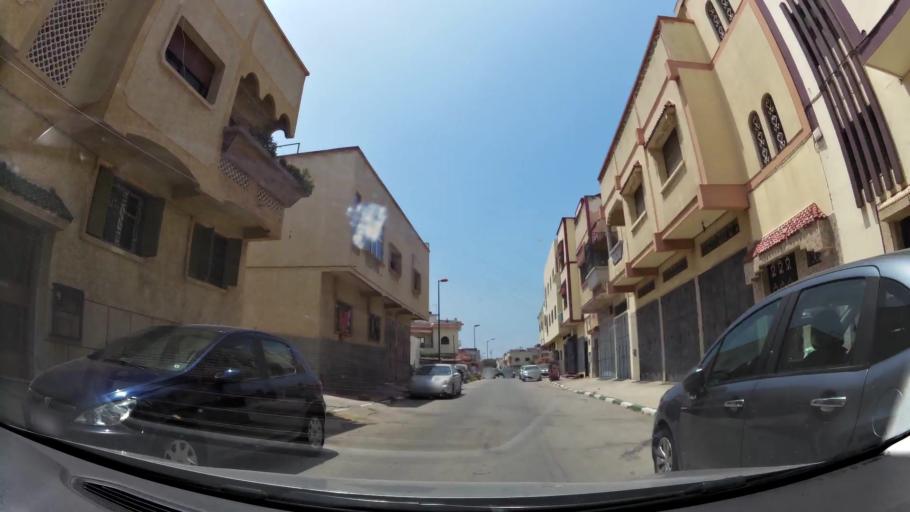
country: MA
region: Rabat-Sale-Zemmour-Zaer
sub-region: Skhirate-Temara
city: Temara
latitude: 33.9796
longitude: -6.8921
